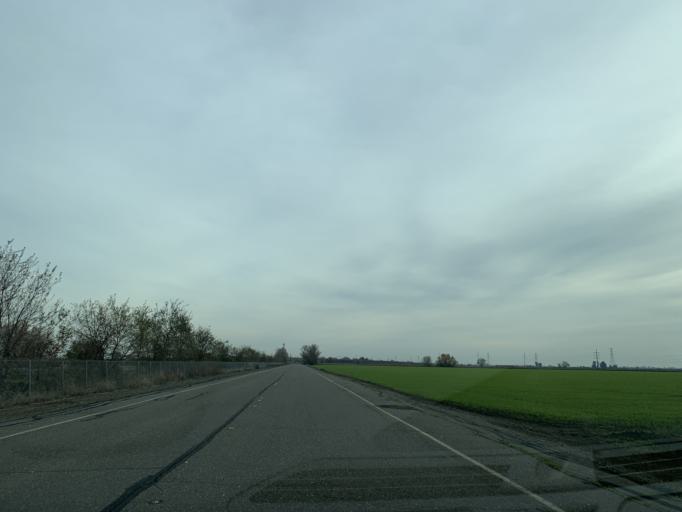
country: US
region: California
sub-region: Yuba County
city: Plumas Lake
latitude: 38.8600
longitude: -121.5502
